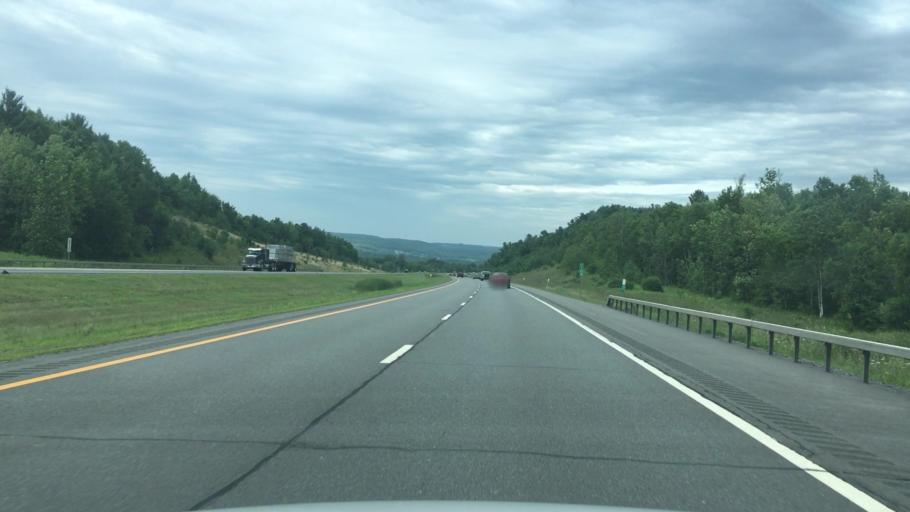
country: US
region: New York
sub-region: Albany County
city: Altamont
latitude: 42.7434
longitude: -74.1642
